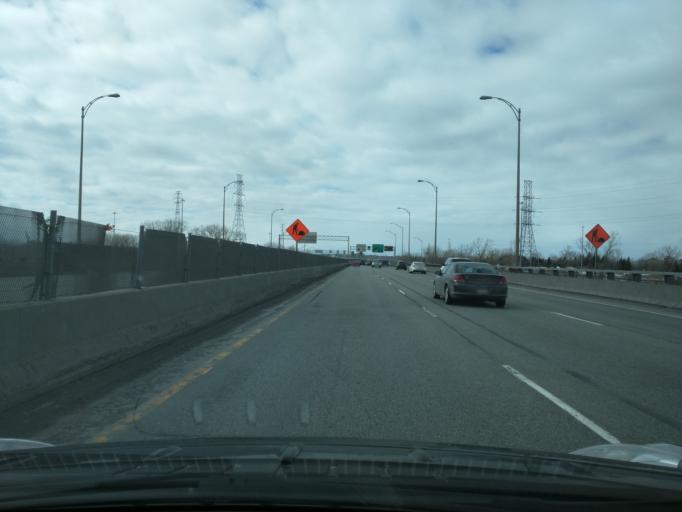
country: CA
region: Quebec
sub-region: Monteregie
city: Boucherville
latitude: 45.5793
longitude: -73.4796
